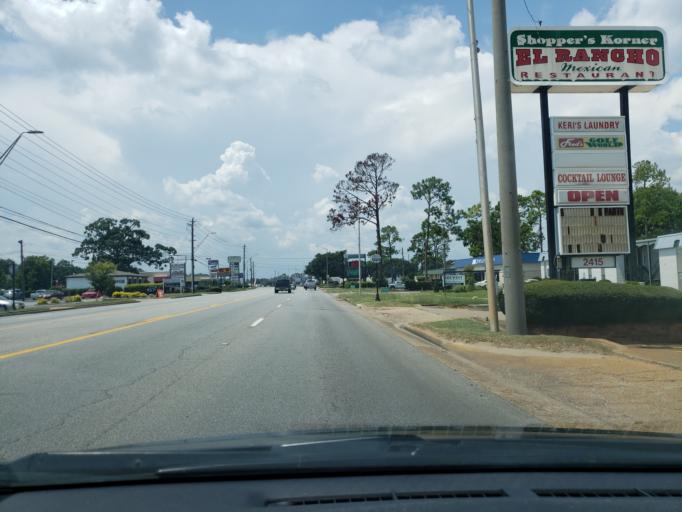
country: US
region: Georgia
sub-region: Dougherty County
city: Albany
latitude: 31.6092
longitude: -84.2102
